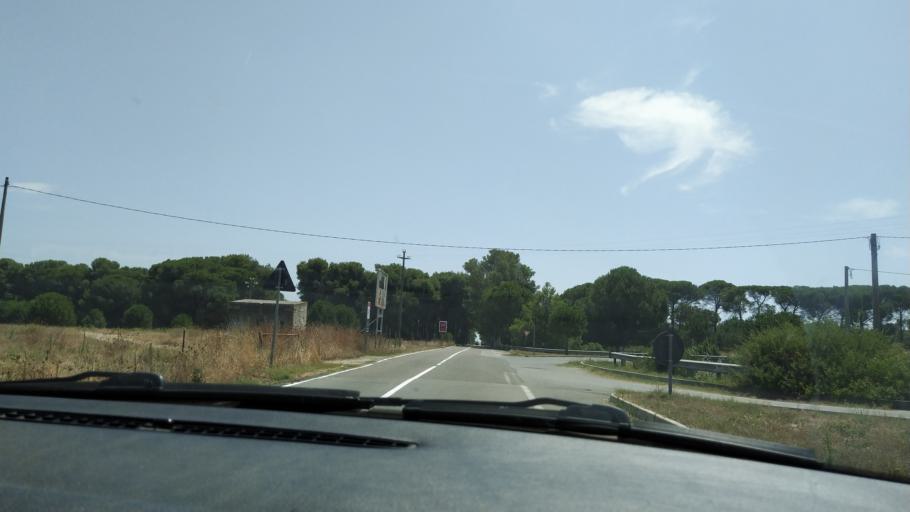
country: IT
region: Basilicate
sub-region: Provincia di Matera
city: Marconia
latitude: 40.3246
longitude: 16.7926
